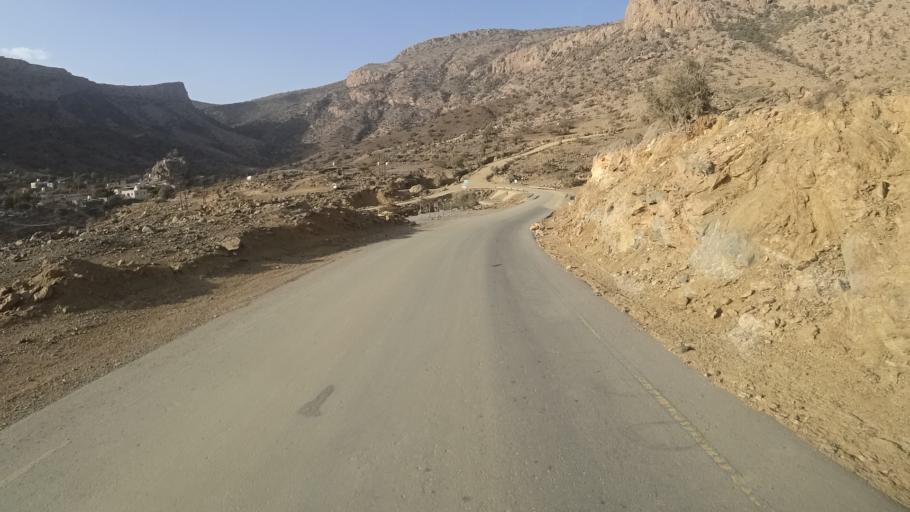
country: OM
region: Al Batinah
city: Rustaq
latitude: 23.2379
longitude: 57.1975
